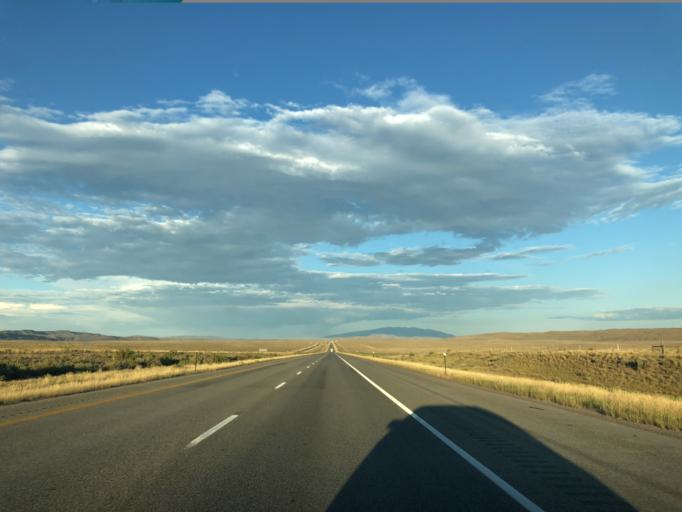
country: US
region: Wyoming
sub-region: Carbon County
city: Rawlins
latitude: 41.7699
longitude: -107.0521
